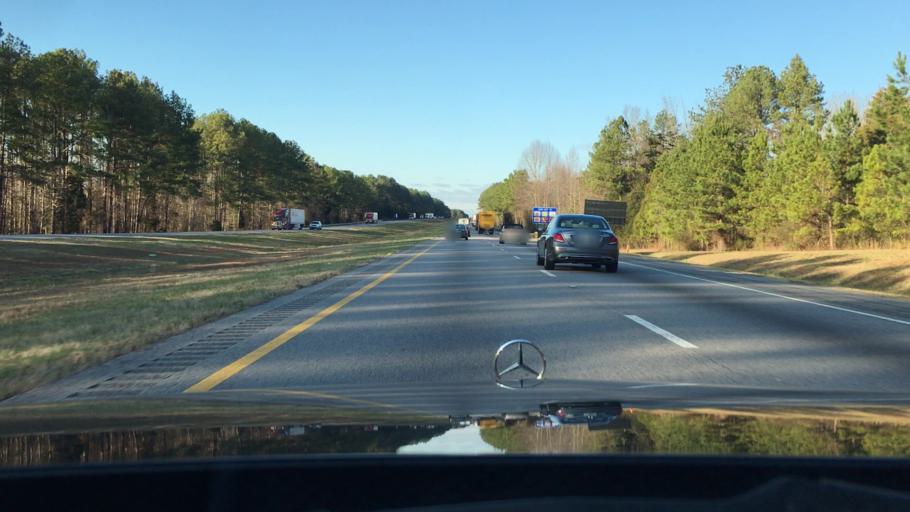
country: US
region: South Carolina
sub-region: Chester County
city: Eureka Mill
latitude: 34.7310
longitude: -81.0338
